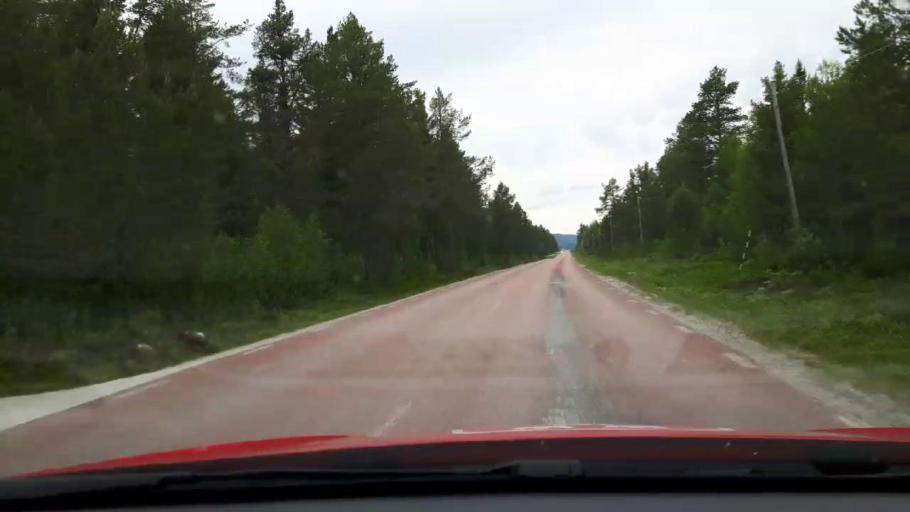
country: NO
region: Hedmark
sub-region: Engerdal
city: Engerdal
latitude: 62.4940
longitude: 12.6363
